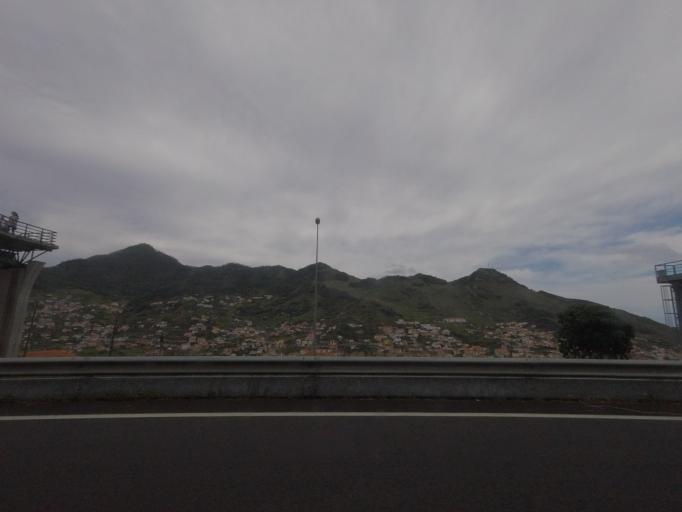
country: PT
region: Madeira
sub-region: Machico
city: Machico
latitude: 32.7213
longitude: -16.7752
